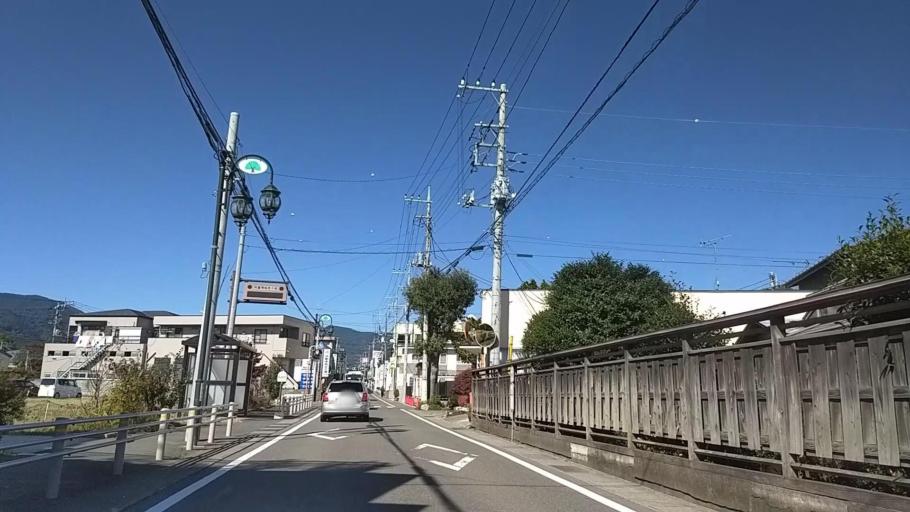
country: JP
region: Yamanashi
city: Uenohara
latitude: 35.6312
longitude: 139.1100
